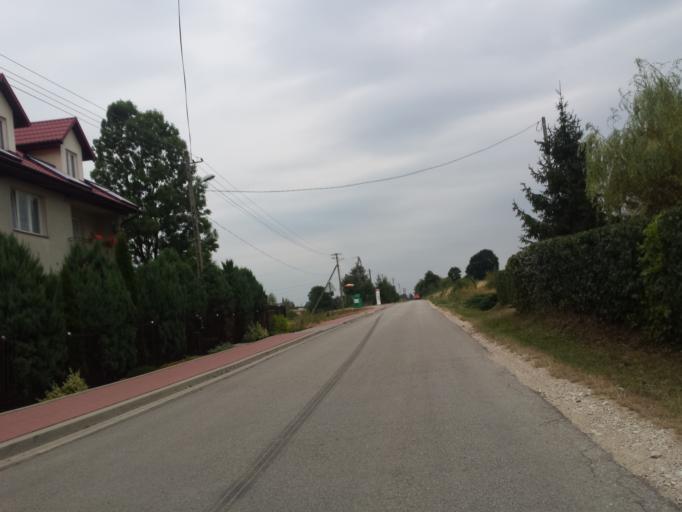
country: PL
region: Swietokrzyskie
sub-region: Powiat kielecki
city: Morawica
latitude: 50.7312
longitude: 20.6829
